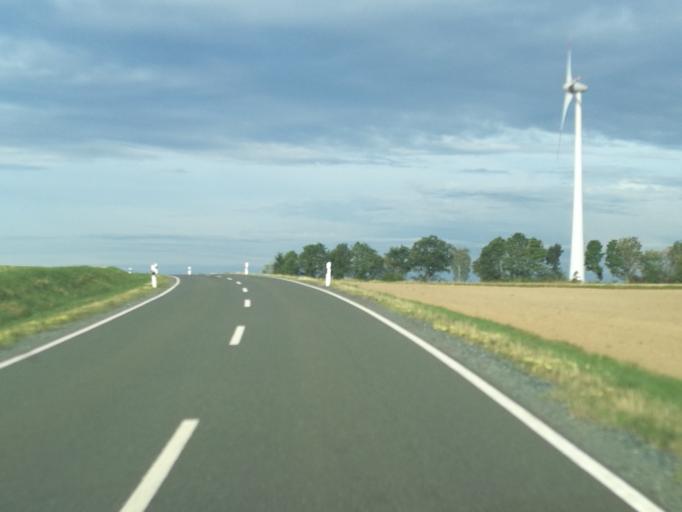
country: DE
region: Bavaria
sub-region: Upper Franconia
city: Gattendorf
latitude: 50.2962
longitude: 12.0044
